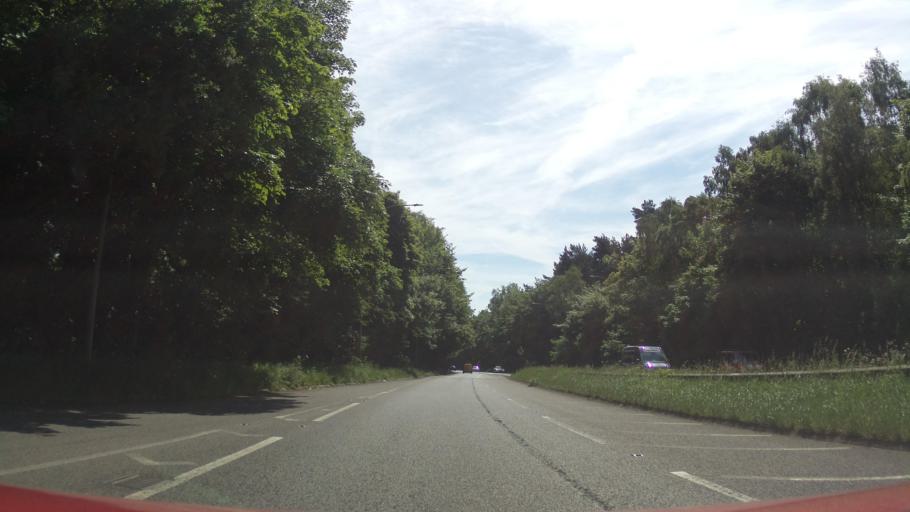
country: GB
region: England
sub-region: North Lincolnshire
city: Broughton
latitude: 53.5522
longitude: -0.5730
